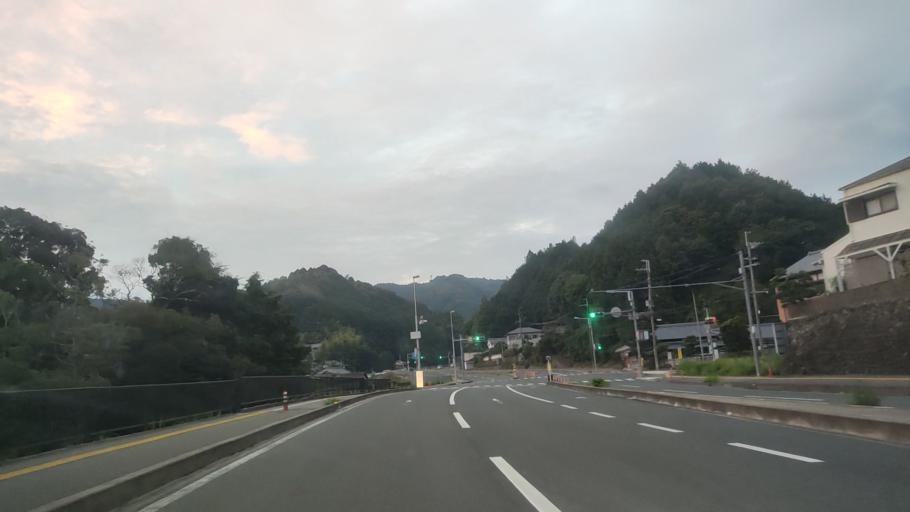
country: JP
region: Wakayama
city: Hashimoto
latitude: 34.3602
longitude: 135.6066
